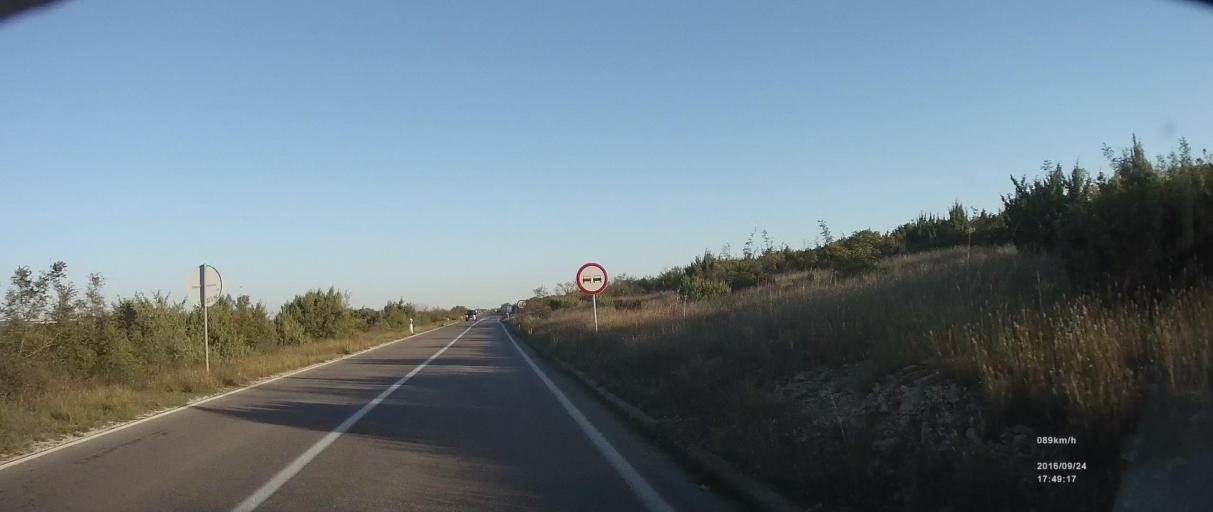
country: HR
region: Zadarska
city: Polaca
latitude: 44.0557
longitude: 15.5478
